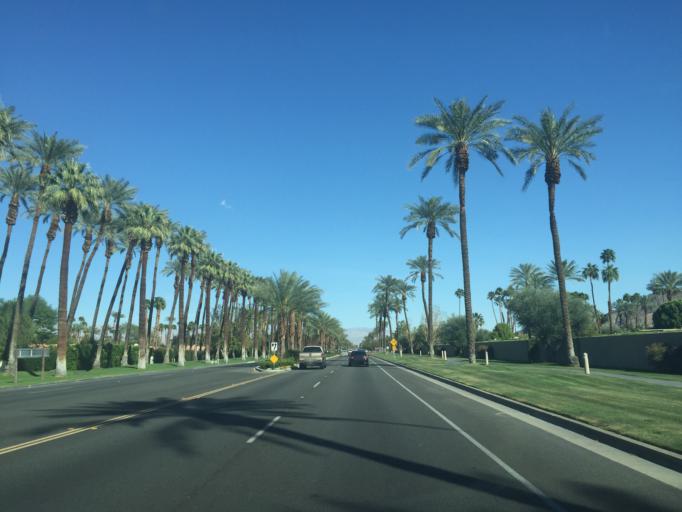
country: US
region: California
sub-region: Riverside County
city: Indian Wells
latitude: 33.7214
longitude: -116.3466
